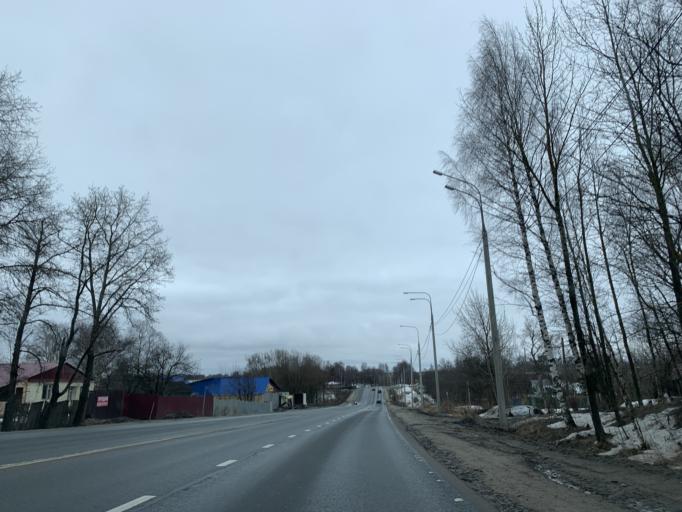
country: RU
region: Jaroslavl
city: Konstantinovskiy
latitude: 57.7637
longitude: 39.6833
